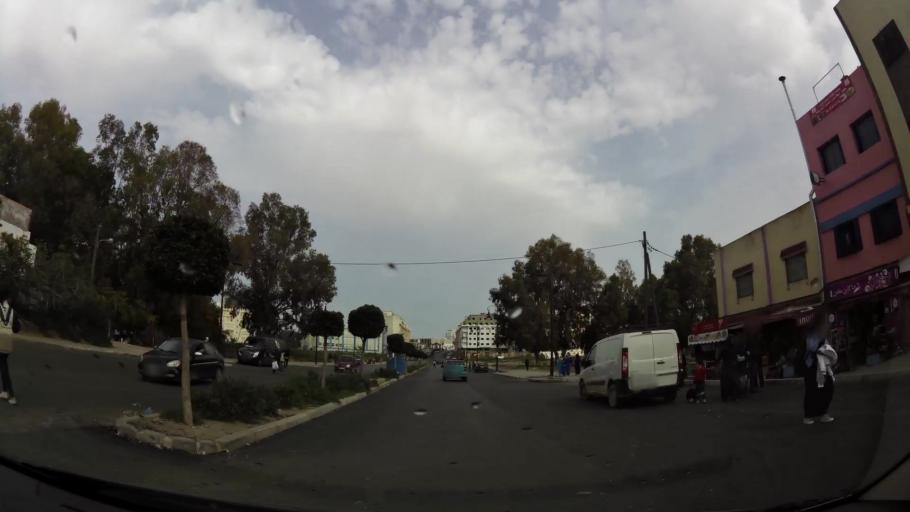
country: MA
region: Tanger-Tetouan
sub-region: Tanger-Assilah
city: Boukhalef
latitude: 35.7373
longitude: -5.8835
